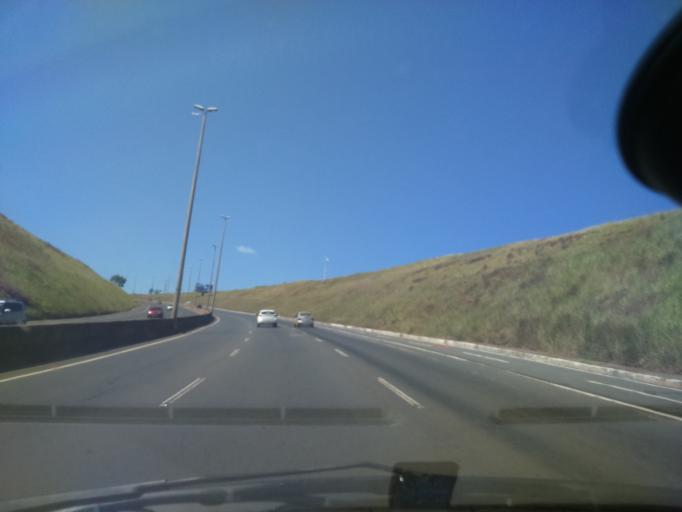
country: BR
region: Federal District
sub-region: Brasilia
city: Brasilia
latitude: -15.8383
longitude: -47.8249
